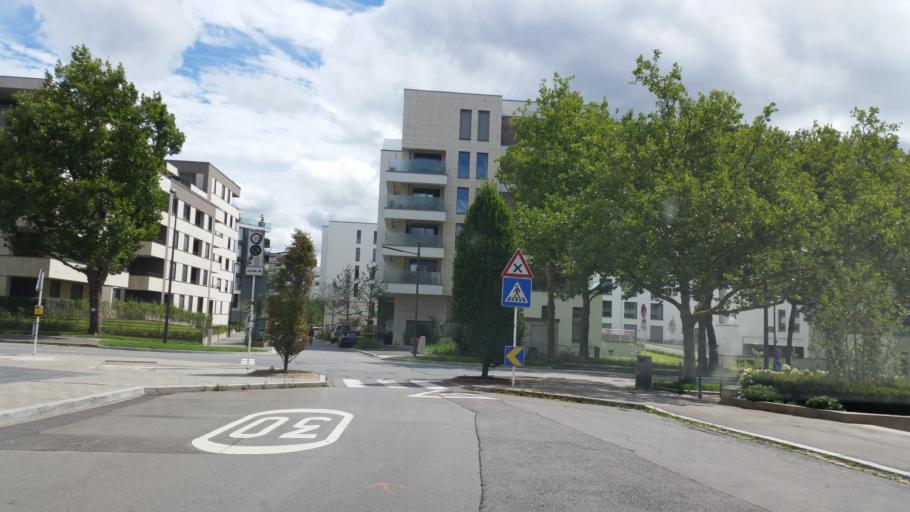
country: LU
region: Luxembourg
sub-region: Canton de Luxembourg
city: Luxembourg
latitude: 49.6044
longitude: 6.1037
